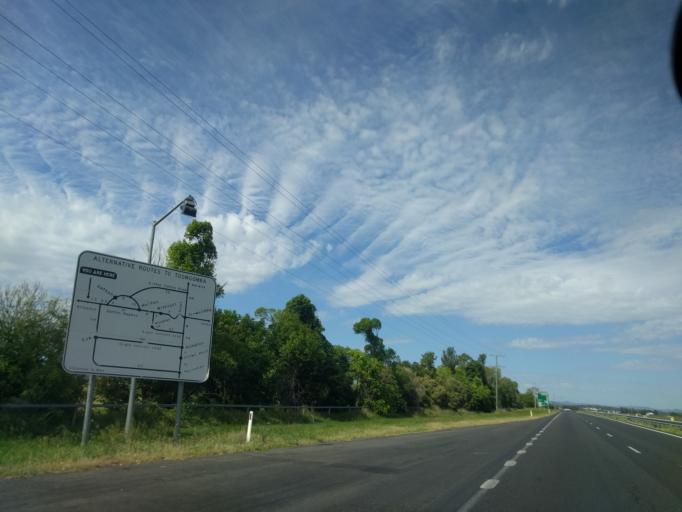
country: AU
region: Queensland
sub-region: Lockyer Valley
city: Gatton
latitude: -27.5490
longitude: 152.3302
